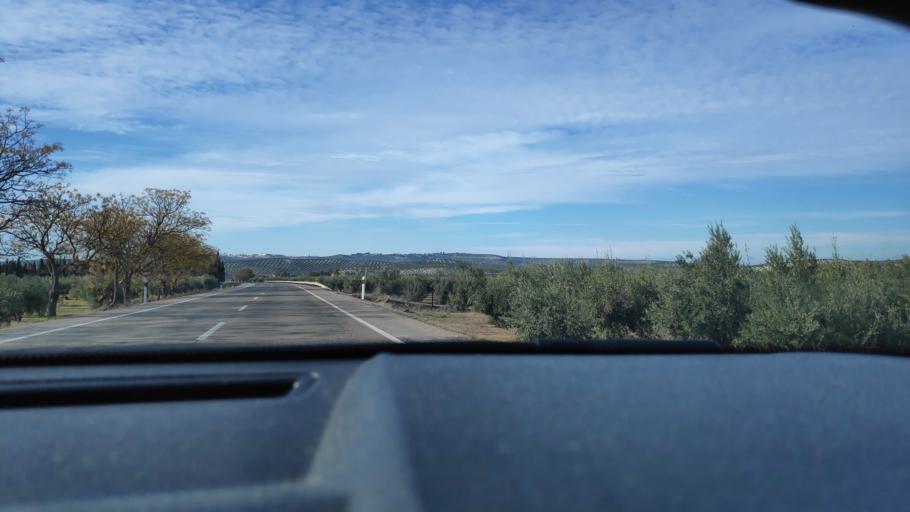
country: ES
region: Andalusia
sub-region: Provincia de Jaen
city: Higuera de Calatrava
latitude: 37.8451
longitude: -4.1187
